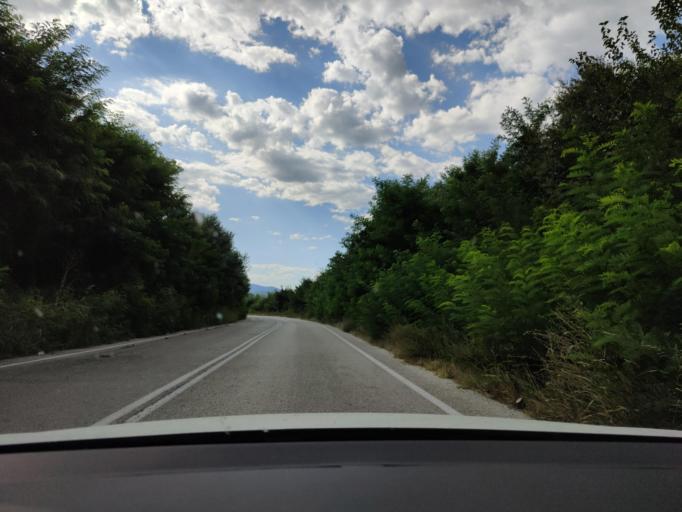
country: GR
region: Central Macedonia
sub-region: Nomos Serron
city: Strymoniko
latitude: 41.0559
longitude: 23.3171
